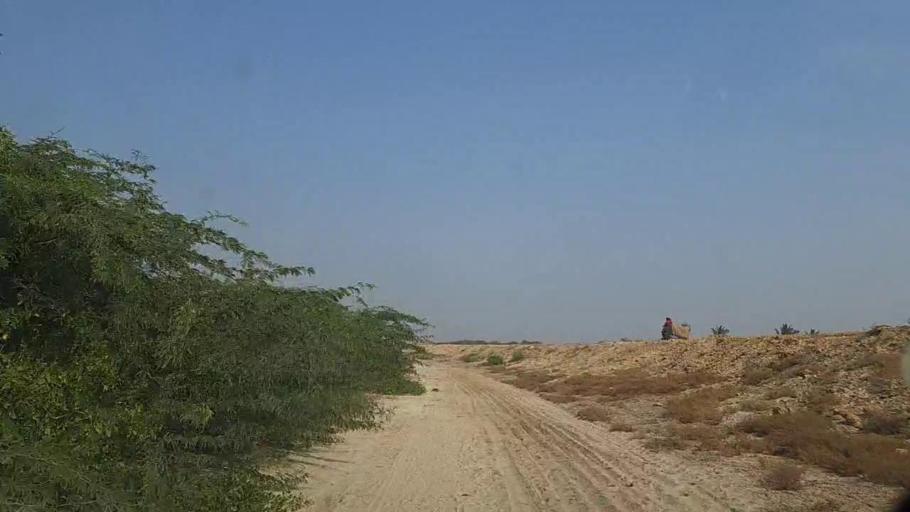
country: PK
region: Sindh
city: Thatta
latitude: 24.6548
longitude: 67.9260
